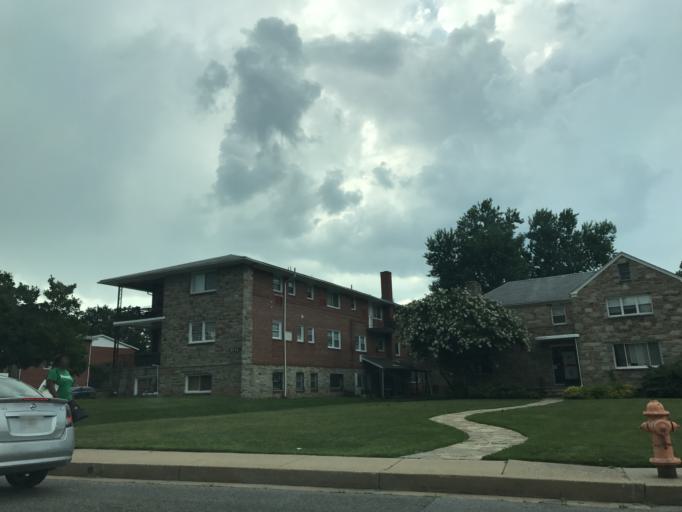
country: US
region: Maryland
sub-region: Baltimore County
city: Pikesville
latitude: 39.3580
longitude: -76.6985
